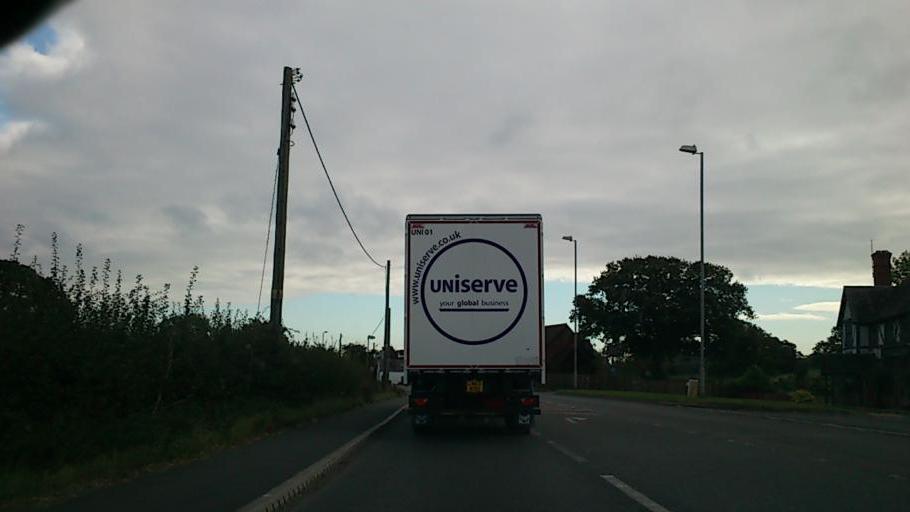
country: GB
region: England
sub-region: Shropshire
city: Ford
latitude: 52.7135
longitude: -2.8603
